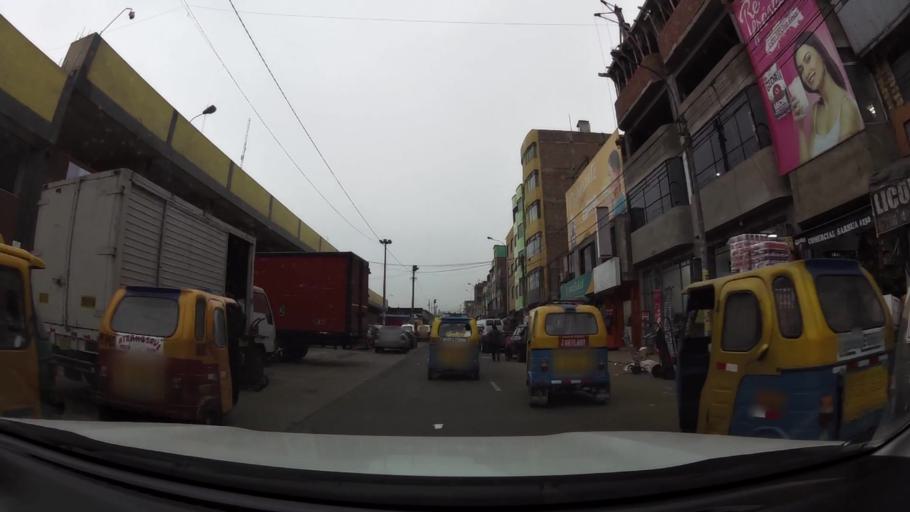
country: PE
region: Lima
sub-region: Lima
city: Surco
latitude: -12.1525
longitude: -76.9705
